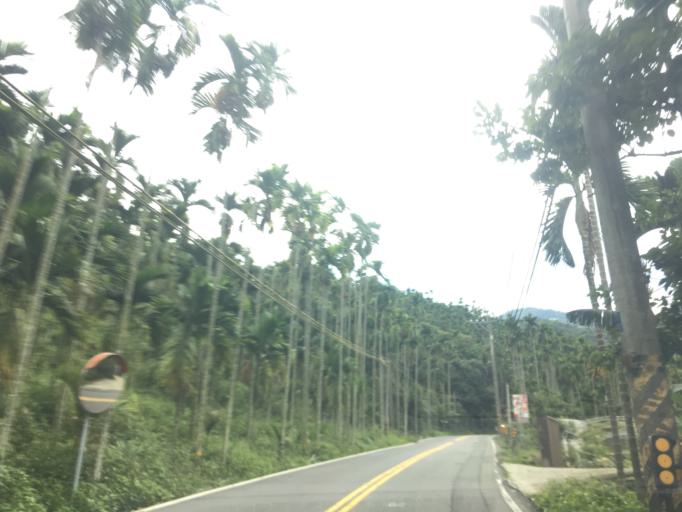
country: TW
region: Taiwan
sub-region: Yunlin
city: Douliu
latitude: 23.5677
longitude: 120.5694
